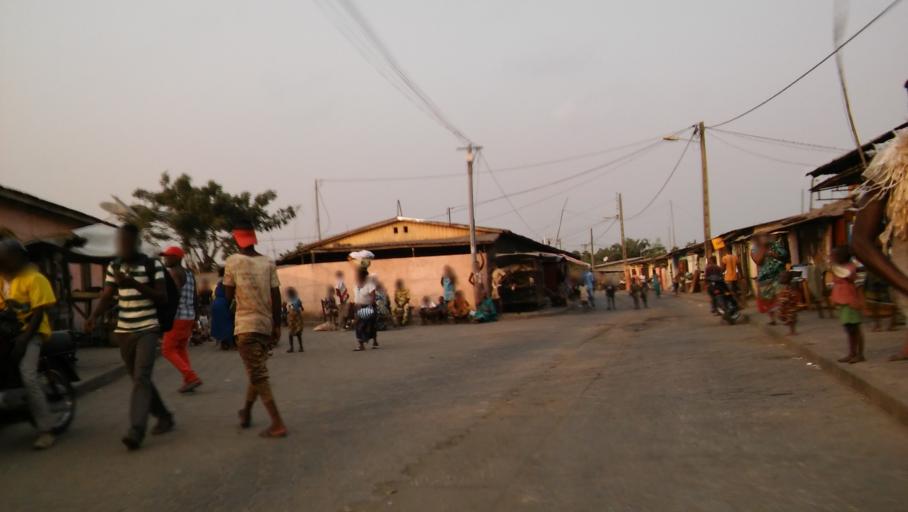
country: BJ
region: Atlantique
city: Abomey-Calavi
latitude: 6.3915
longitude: 2.3466
